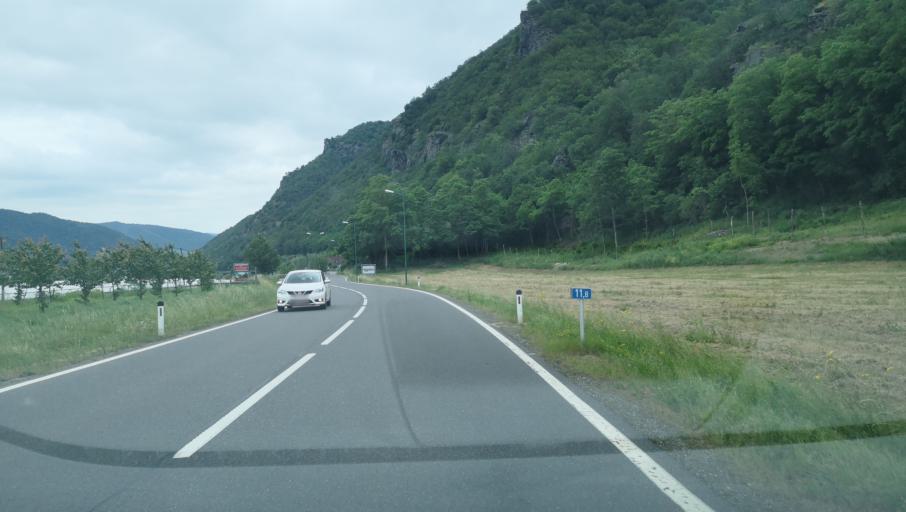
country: AT
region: Lower Austria
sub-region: Politischer Bezirk Krems
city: Aggsbach
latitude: 48.3138
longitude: 15.4134
